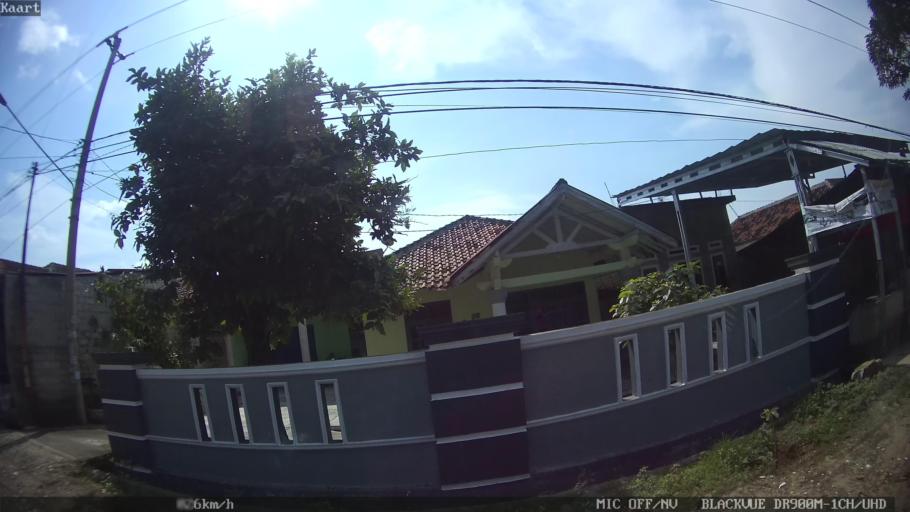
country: ID
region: Lampung
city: Kedaton
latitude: -5.3993
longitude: 105.2347
